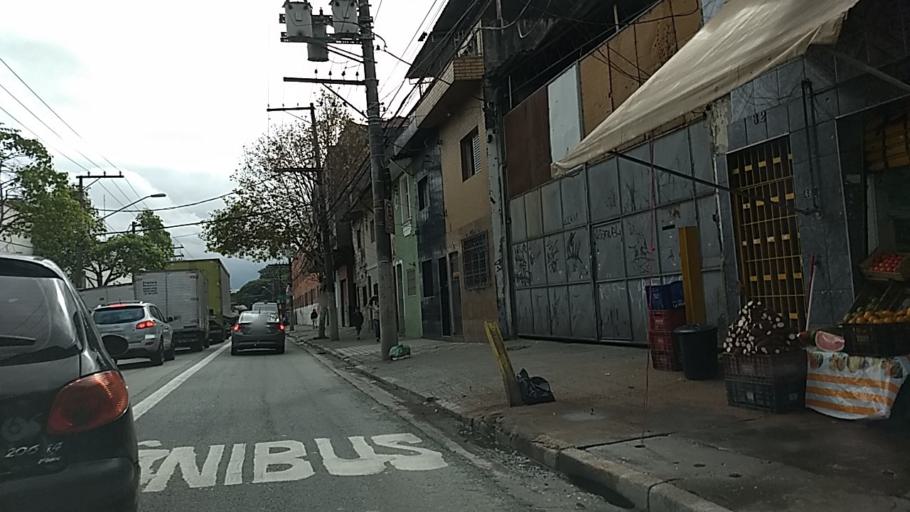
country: BR
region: Sao Paulo
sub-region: Sao Paulo
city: Sao Paulo
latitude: -23.5324
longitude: -46.6014
